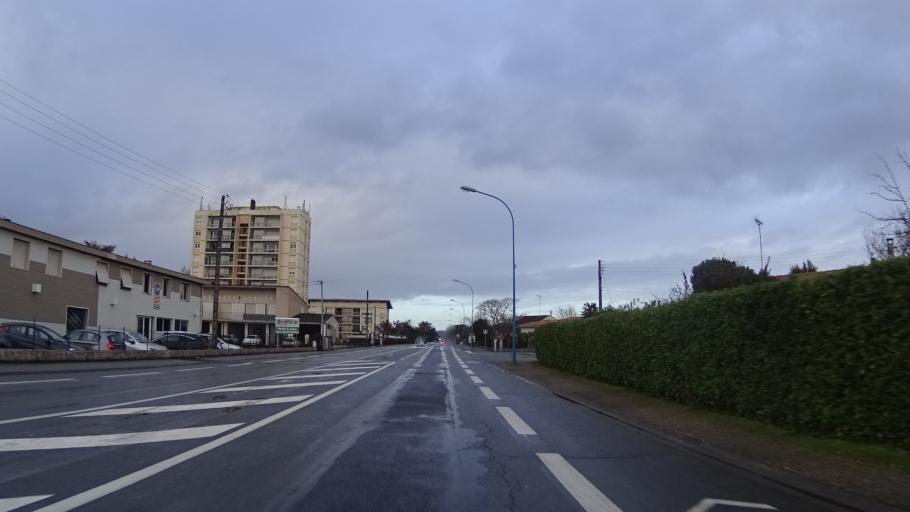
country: FR
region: Aquitaine
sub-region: Departement du Lot-et-Garonne
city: Le Passage
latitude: 44.1813
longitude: 0.6045
